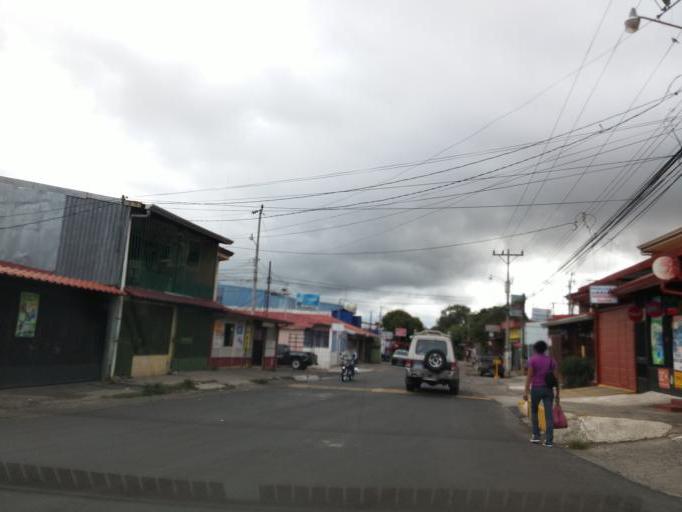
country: CR
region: Alajuela
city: Alajuela
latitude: 10.0026
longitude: -84.2161
